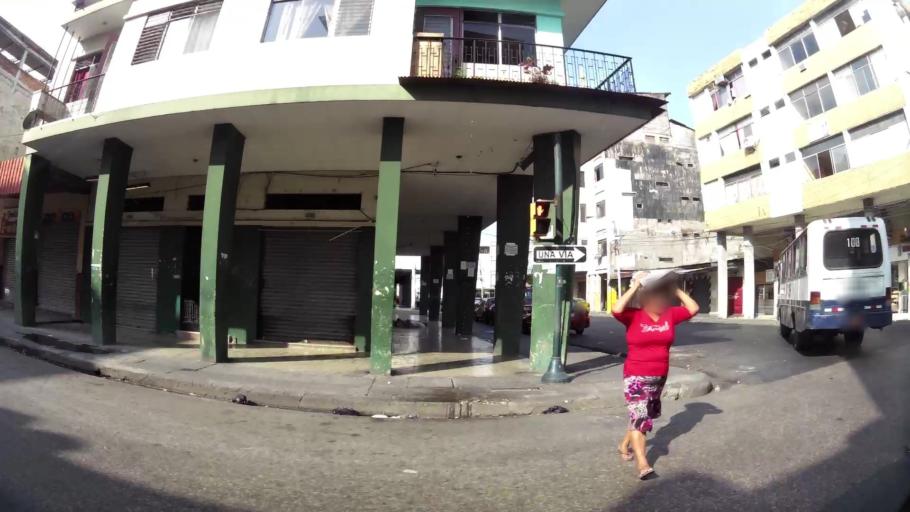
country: EC
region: Guayas
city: Guayaquil
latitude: -2.1957
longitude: -79.8884
